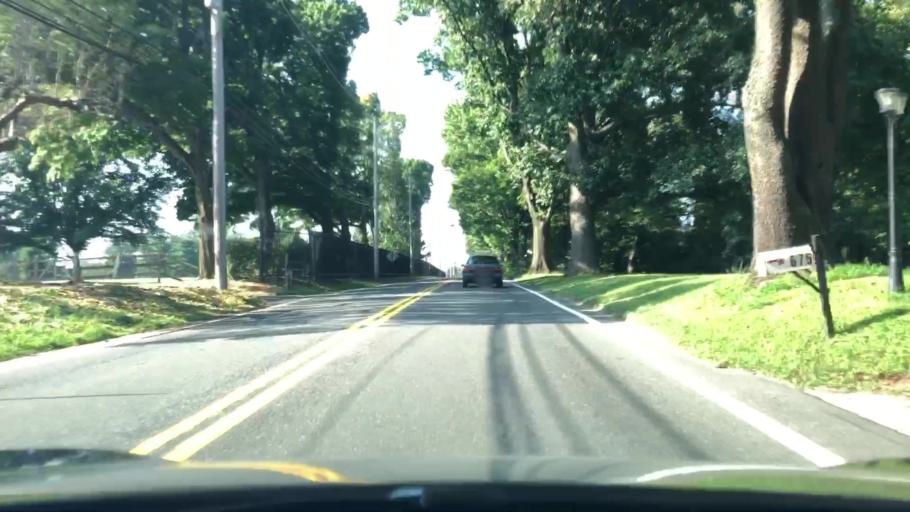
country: US
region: Pennsylvania
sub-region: Delaware County
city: Broomall
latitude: 40.0134
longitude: -75.3661
